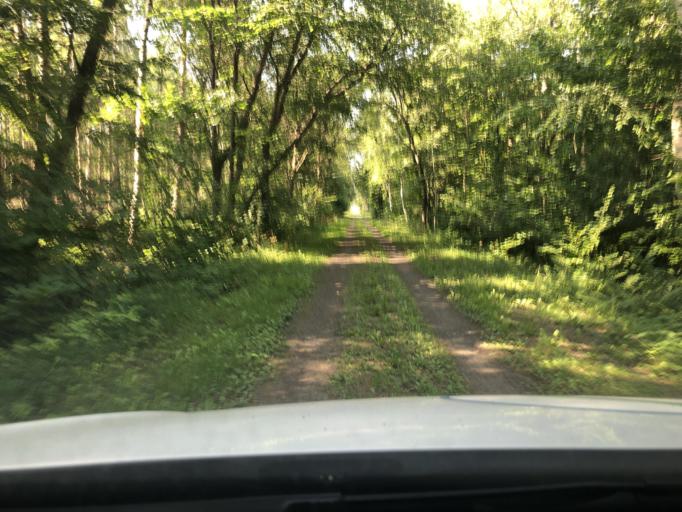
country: SE
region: Skane
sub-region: Kristianstads Kommun
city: Degeberga
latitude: 55.8077
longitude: 14.1345
